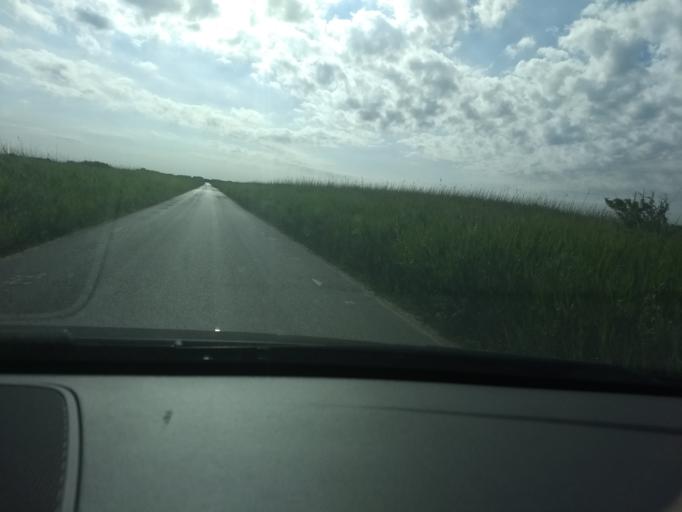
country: DE
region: Schleswig-Holstein
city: List
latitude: 55.1319
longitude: 8.4959
